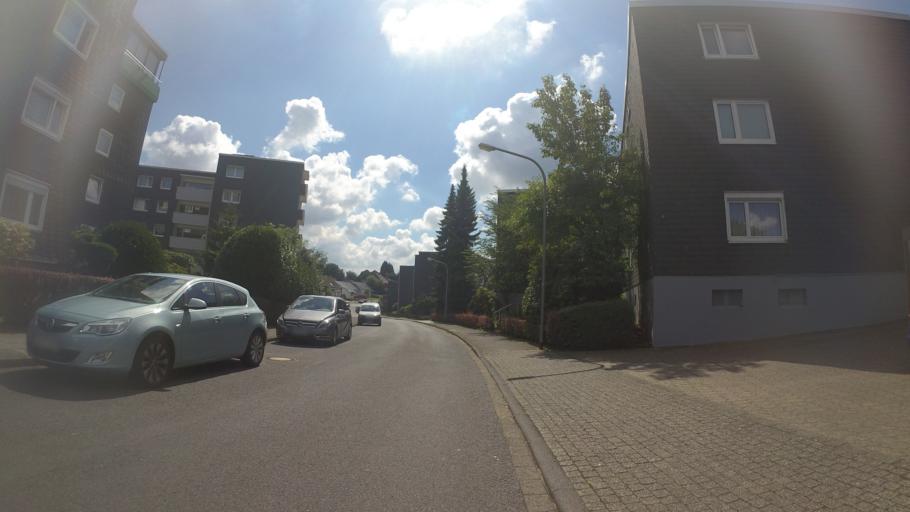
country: DE
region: North Rhine-Westphalia
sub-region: Regierungsbezirk Dusseldorf
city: Remscheid
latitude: 51.2113
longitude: 7.2423
